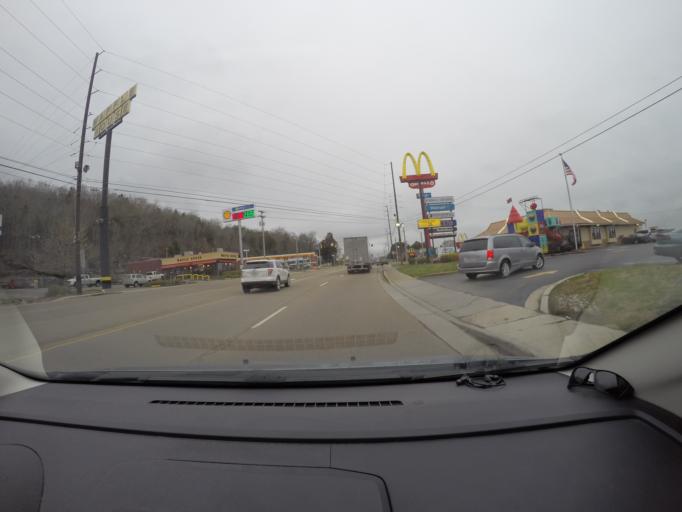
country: US
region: Tennessee
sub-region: Marion County
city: Kimball
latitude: 35.0432
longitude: -85.6866
